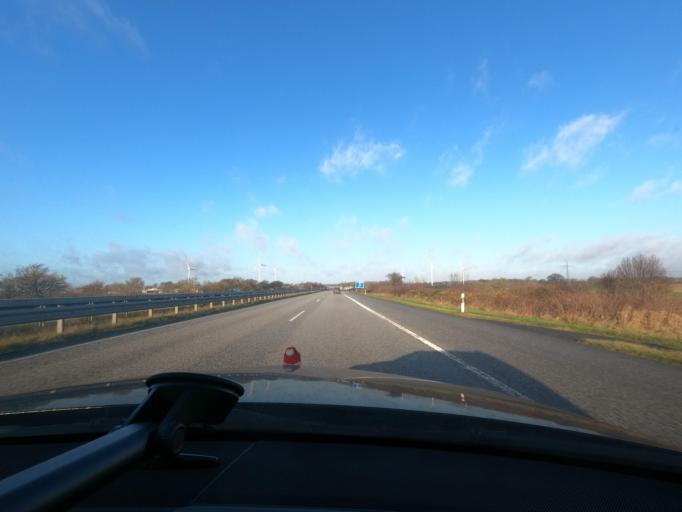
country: DE
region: Schleswig-Holstein
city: Bollingstedt
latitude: 54.6303
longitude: 9.4403
